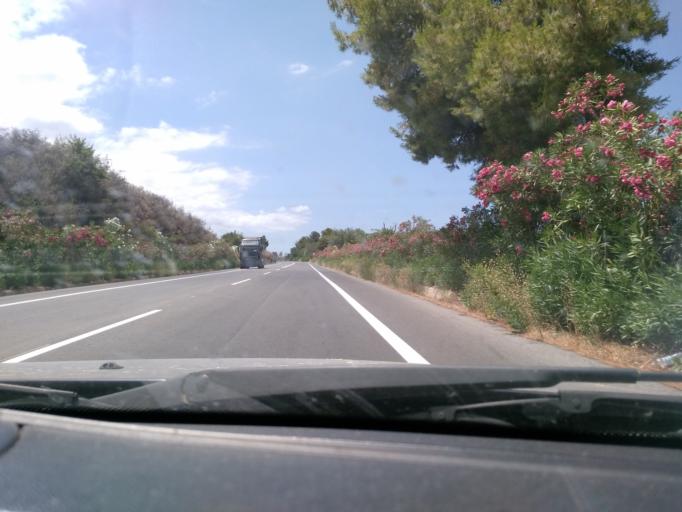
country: GR
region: Crete
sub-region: Nomos Chanias
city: Georgioupolis
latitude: 35.3652
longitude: 24.2344
